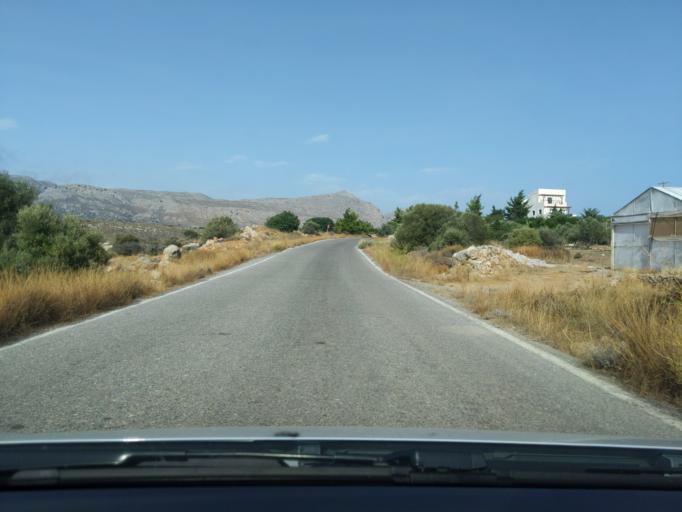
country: GR
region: Crete
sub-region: Nomos Lasithiou
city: Palekastro
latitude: 35.0850
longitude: 26.2455
